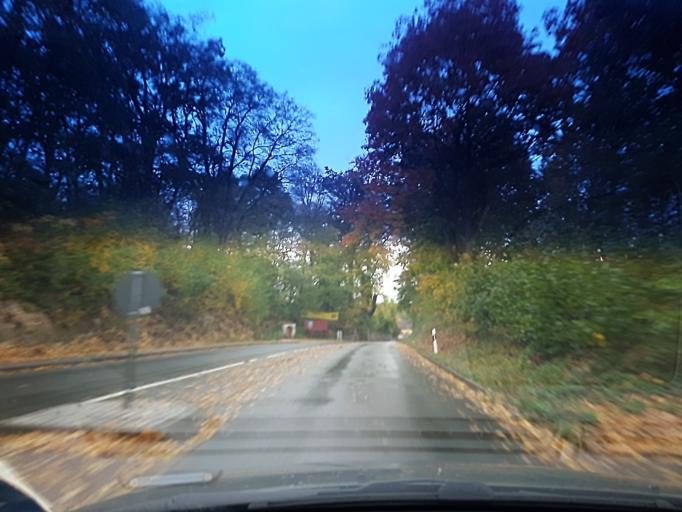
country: DE
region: Bavaria
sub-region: Upper Franconia
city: Pommersfelden
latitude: 49.7705
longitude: 10.8020
